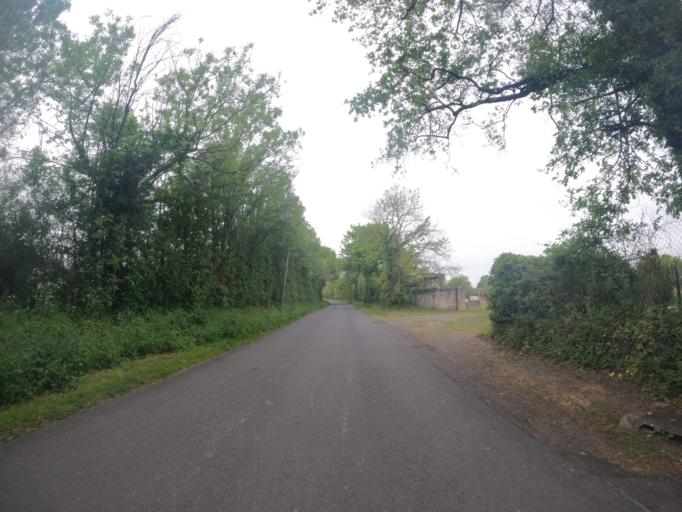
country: FR
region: Poitou-Charentes
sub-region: Departement des Deux-Sevres
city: Chiche
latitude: 46.8281
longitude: -0.3606
